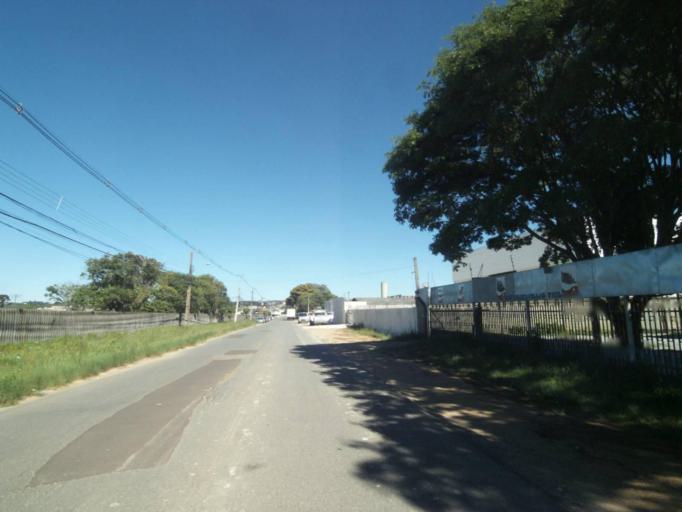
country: BR
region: Parana
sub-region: Curitiba
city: Curitiba
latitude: -25.5004
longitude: -49.3319
